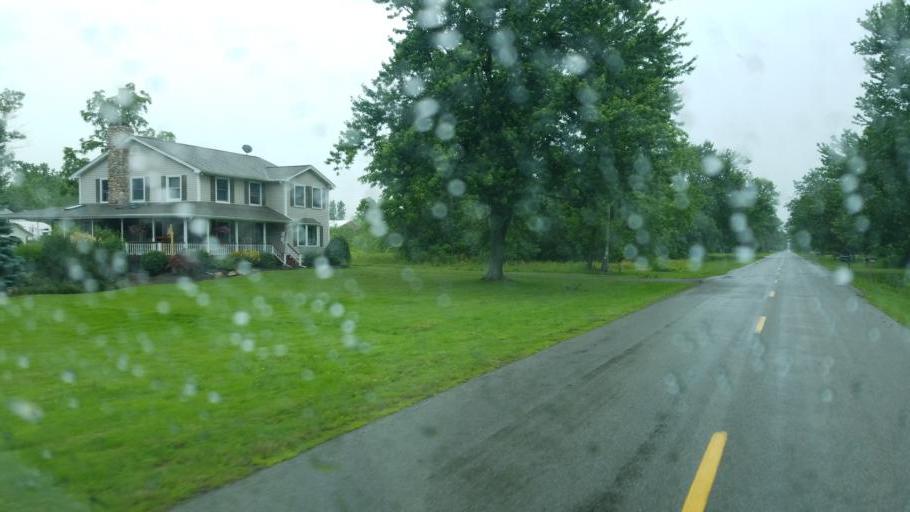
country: US
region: New York
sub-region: Niagara County
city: Wilson
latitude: 43.2644
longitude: -78.8324
